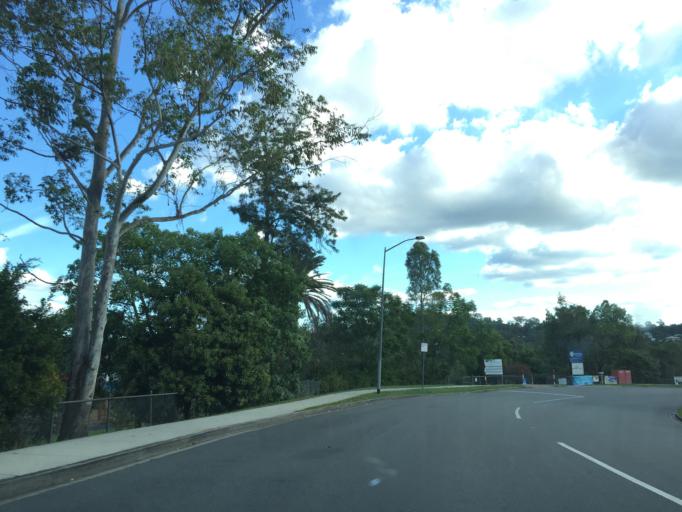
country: AU
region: Queensland
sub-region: Moreton Bay
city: Ferny Hills
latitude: -27.4365
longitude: 152.9379
